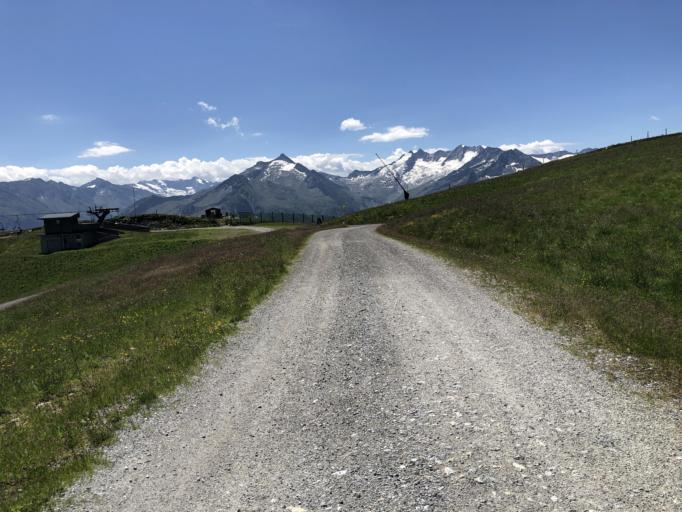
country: AT
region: Salzburg
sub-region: Politischer Bezirk Zell am See
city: Krimml
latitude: 47.2599
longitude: 12.0955
